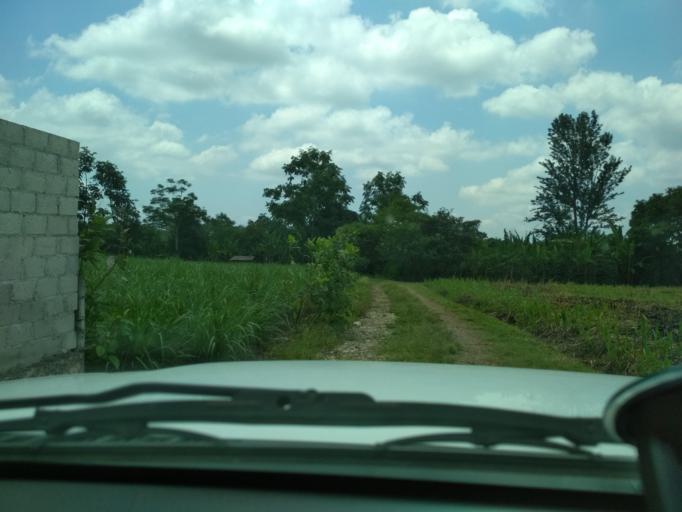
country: MX
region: Veracruz
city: Tocuila
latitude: 18.9556
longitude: -97.0137
